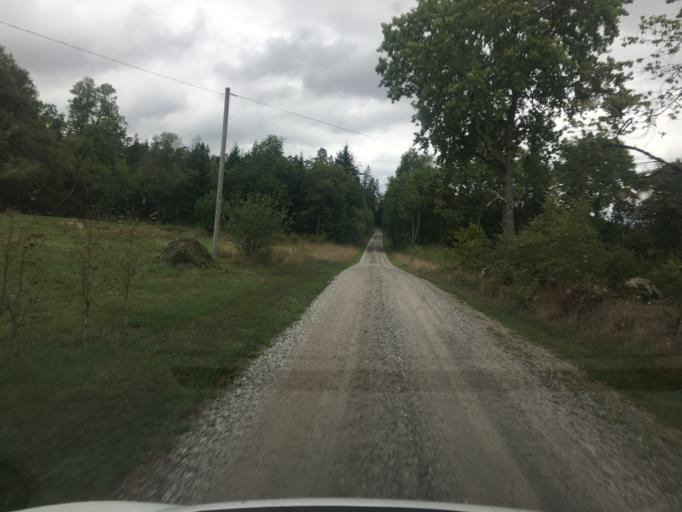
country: SE
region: Kronoberg
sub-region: Ljungby Kommun
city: Lagan
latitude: 56.9572
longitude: 14.0420
